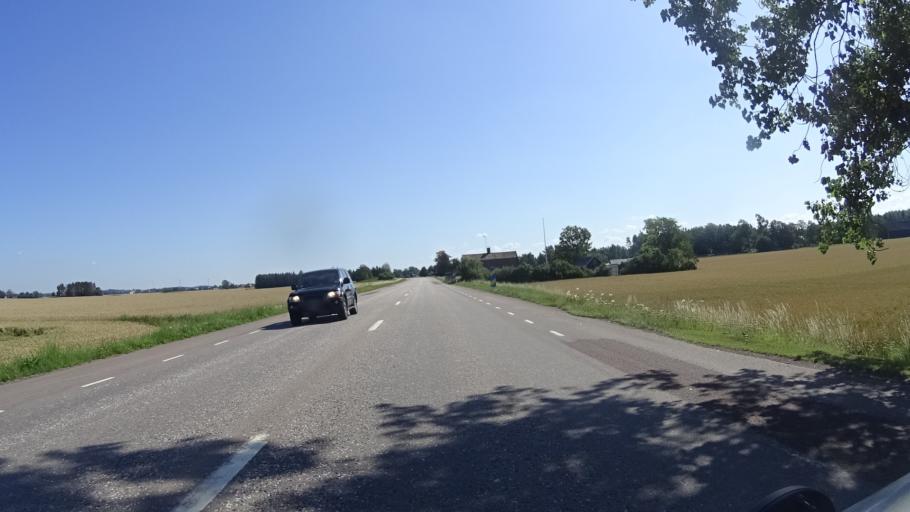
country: SE
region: OEstergoetland
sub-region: Vadstena Kommun
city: Herrestad
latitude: 58.3102
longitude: 14.8858
